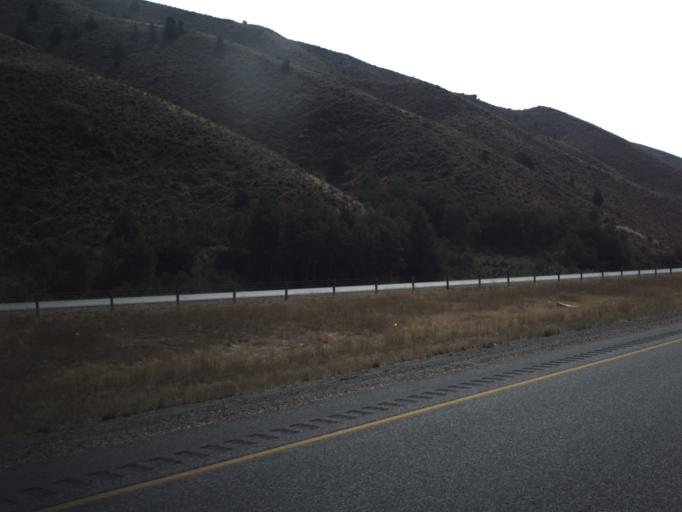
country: US
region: Utah
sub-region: Summit County
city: Coalville
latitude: 41.0754
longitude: -111.2554
